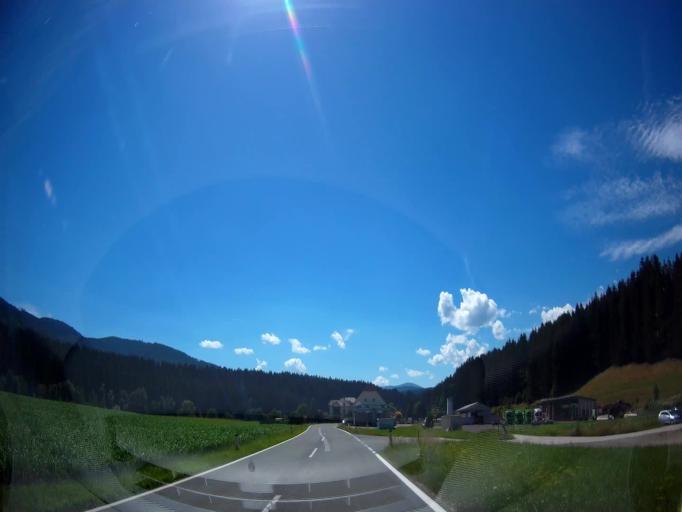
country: AT
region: Carinthia
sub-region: Politischer Bezirk Sankt Veit an der Glan
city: Glodnitz
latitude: 46.8513
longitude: 14.1551
